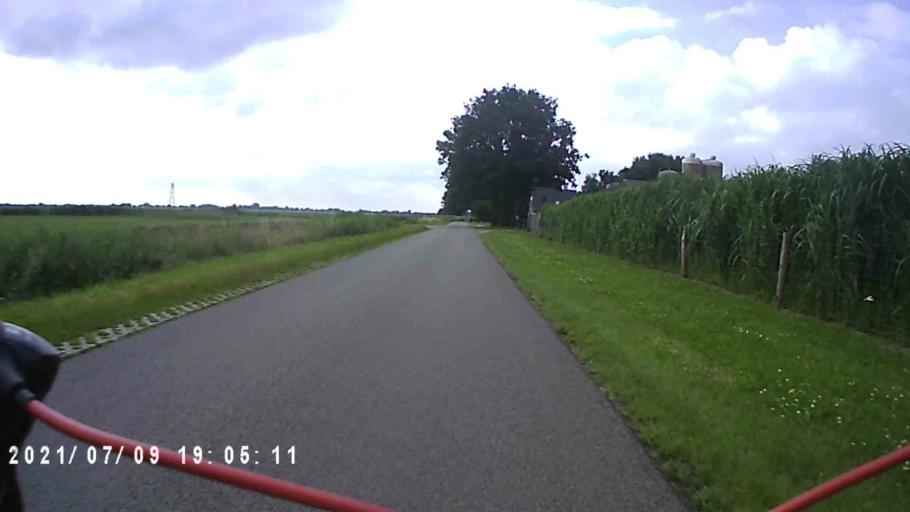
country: NL
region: Groningen
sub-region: Gemeente Veendam
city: Veendam
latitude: 53.0535
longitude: 6.8840
